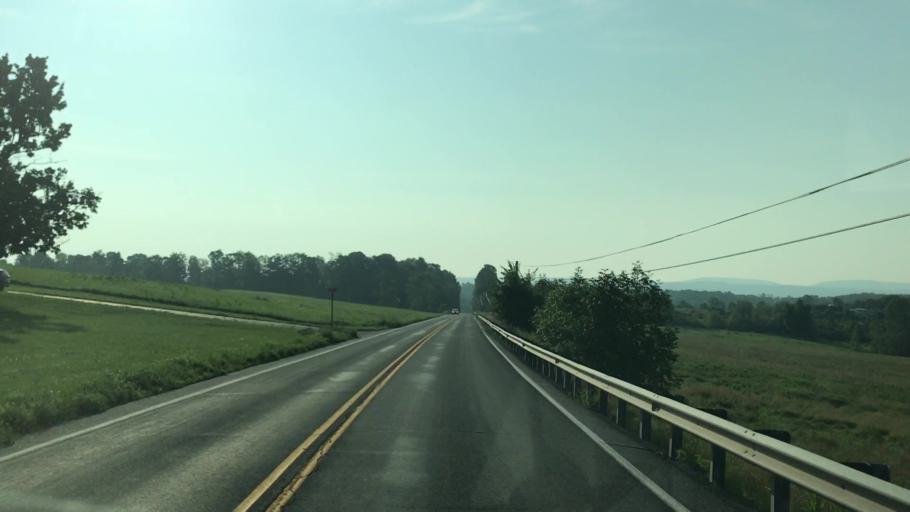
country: US
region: Pennsylvania
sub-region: Lackawanna County
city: Dalton
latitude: 41.6001
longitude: -75.6831
